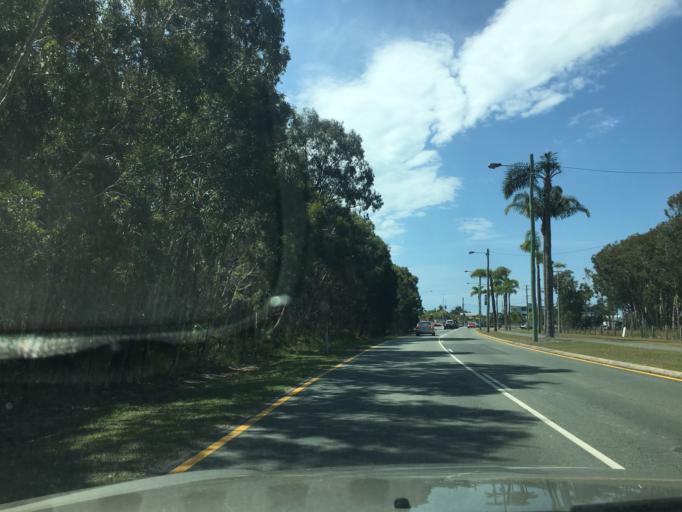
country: AU
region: Queensland
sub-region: Moreton Bay
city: Bongaree
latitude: -27.0762
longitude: 153.1371
